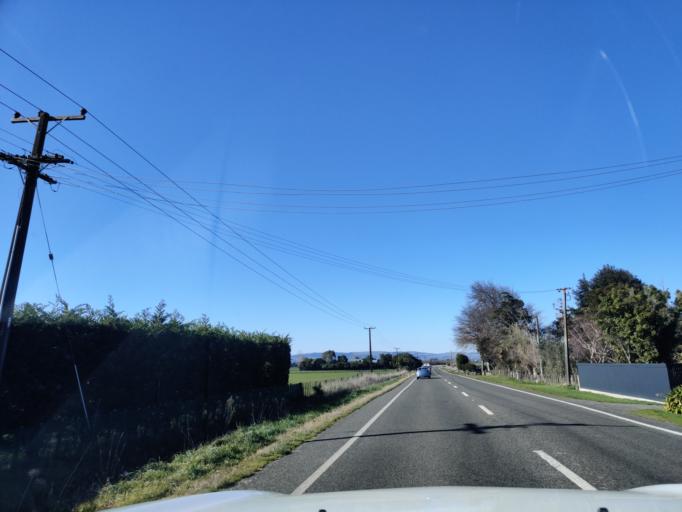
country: NZ
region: Manawatu-Wanganui
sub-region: Palmerston North City
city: Palmerston North
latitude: -40.2828
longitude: 175.5583
